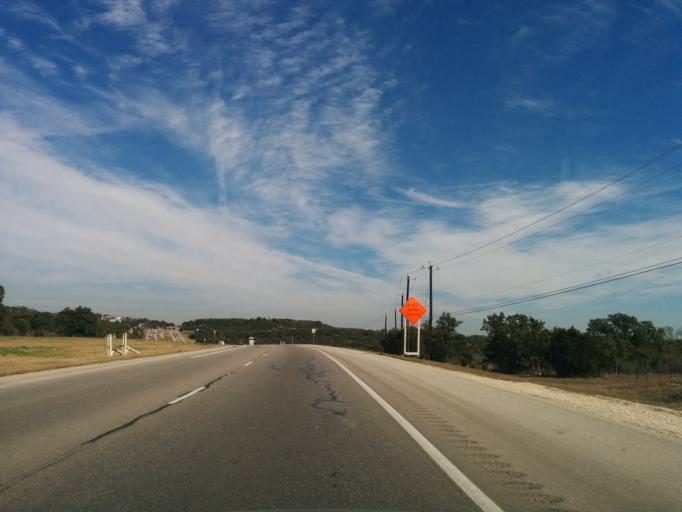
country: US
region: Texas
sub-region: Comal County
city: Bulverde
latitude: 29.7653
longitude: -98.4285
